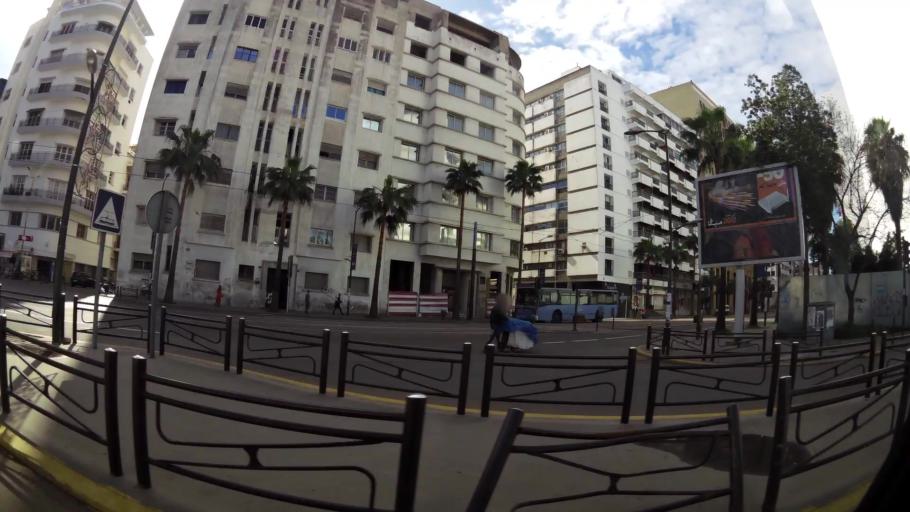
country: MA
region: Grand Casablanca
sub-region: Casablanca
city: Casablanca
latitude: 33.5860
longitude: -7.6224
